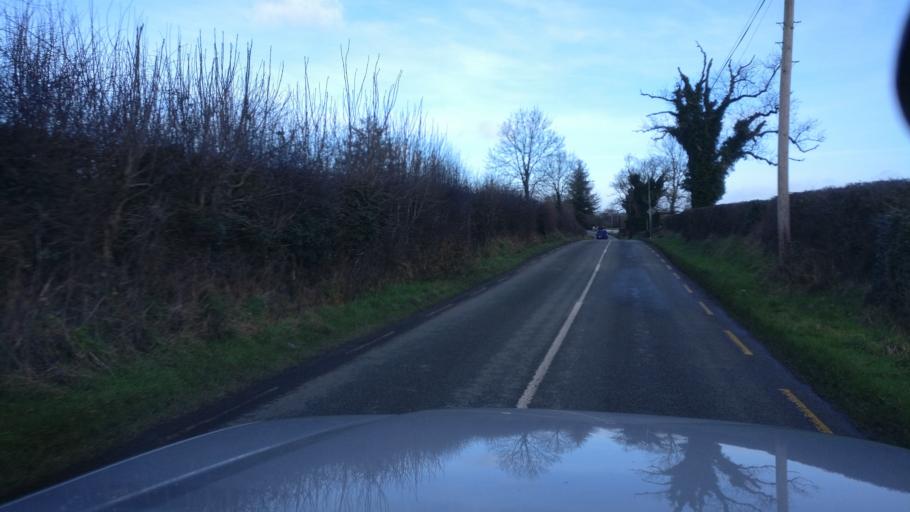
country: IE
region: Leinster
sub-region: Kilkenny
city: Castlecomer
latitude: 52.8320
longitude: -7.1981
